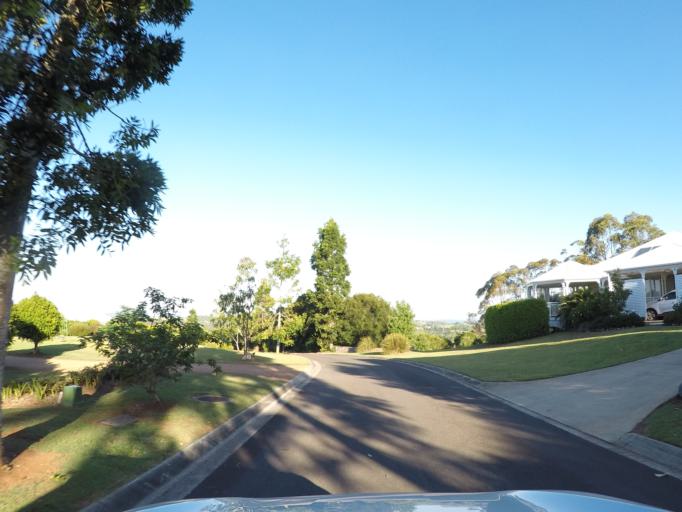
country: AU
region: Queensland
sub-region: Sunshine Coast
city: Nambour
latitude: -26.6302
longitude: 152.8704
